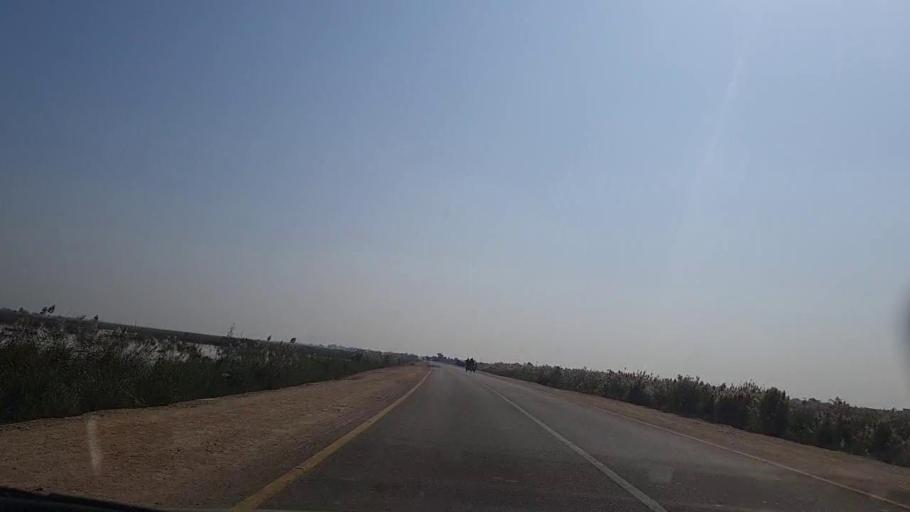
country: PK
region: Sindh
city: Sakrand
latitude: 26.0807
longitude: 68.4027
